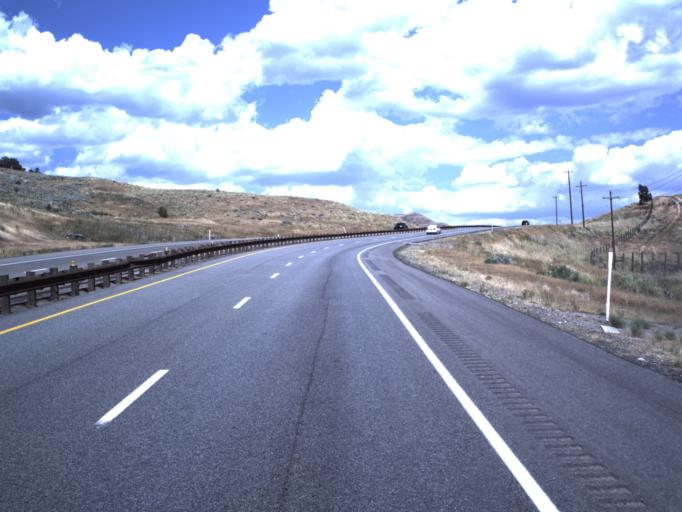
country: US
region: Utah
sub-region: Wasatch County
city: Midway
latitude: 40.3858
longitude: -111.5511
